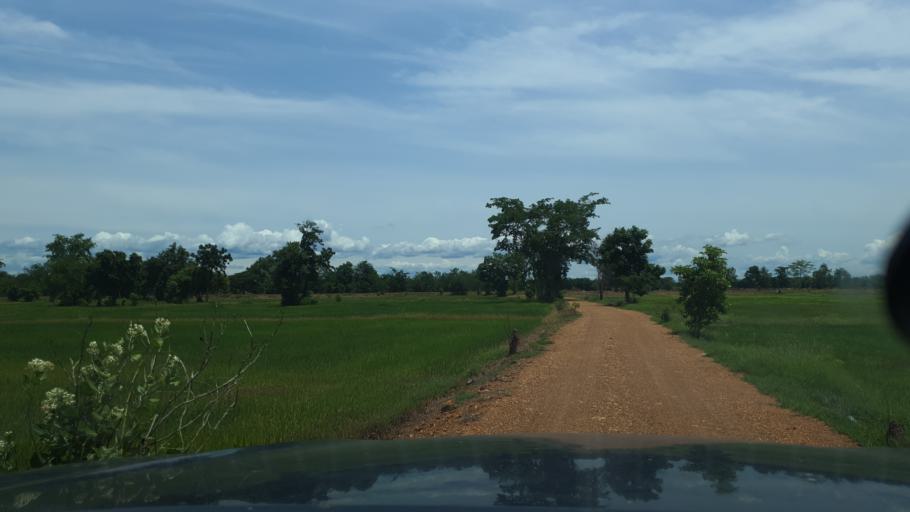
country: TH
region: Sukhothai
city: Ban Na
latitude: 17.0779
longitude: 99.6932
